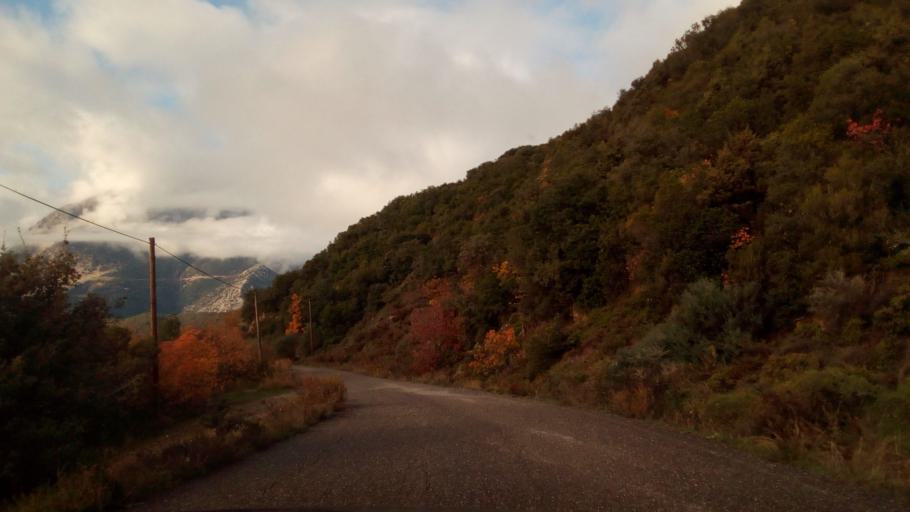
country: GR
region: West Greece
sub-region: Nomos Aitolias kai Akarnanias
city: Nafpaktos
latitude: 38.5142
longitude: 21.9608
